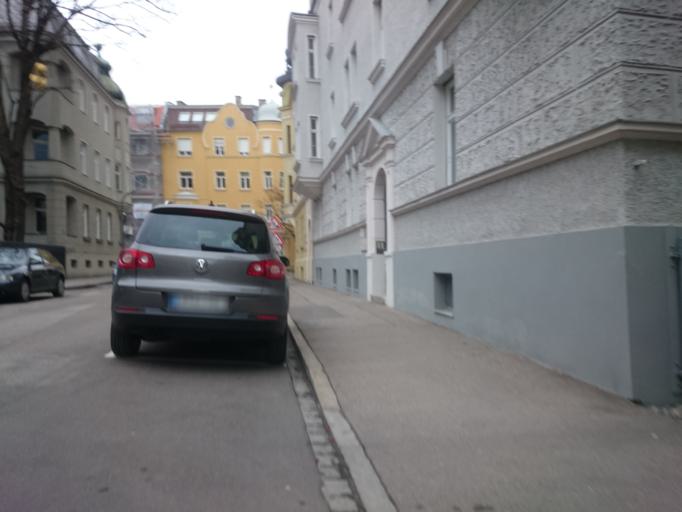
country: DE
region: Bavaria
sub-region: Swabia
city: Augsburg
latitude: 48.3612
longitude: 10.8932
